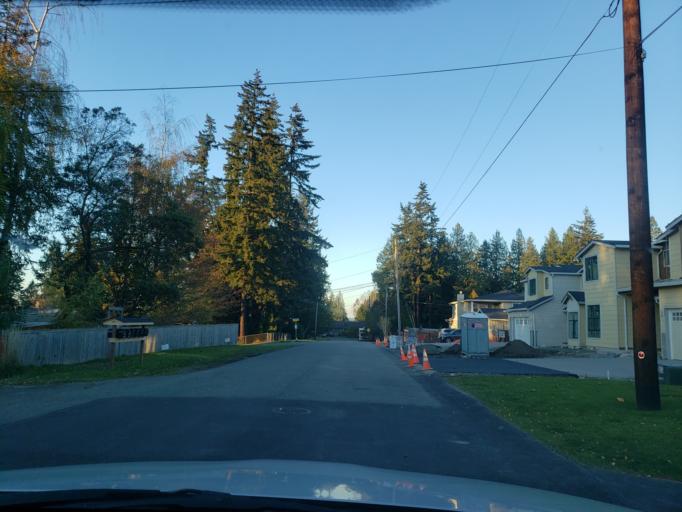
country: US
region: Washington
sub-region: Snohomish County
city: Edmonds
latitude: 47.8034
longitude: -122.3642
